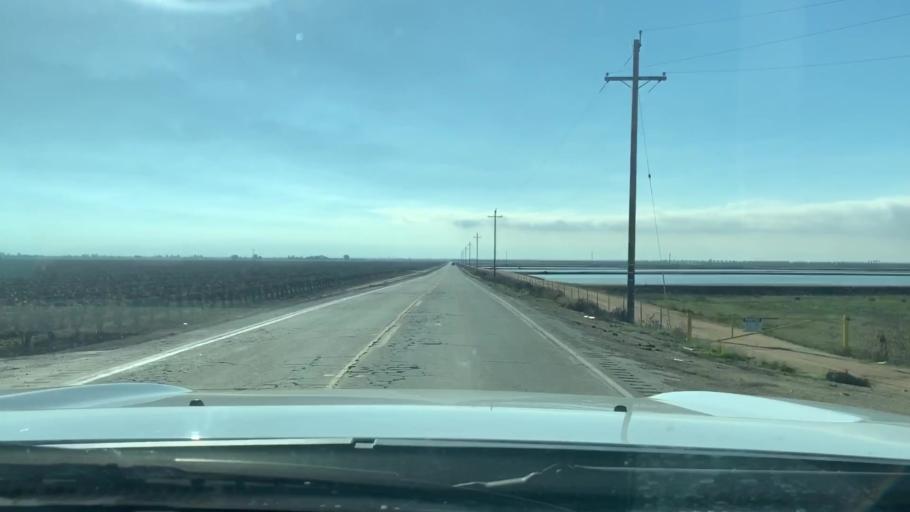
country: US
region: California
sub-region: Kern County
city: Rosedale
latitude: 35.4680
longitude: -119.1535
